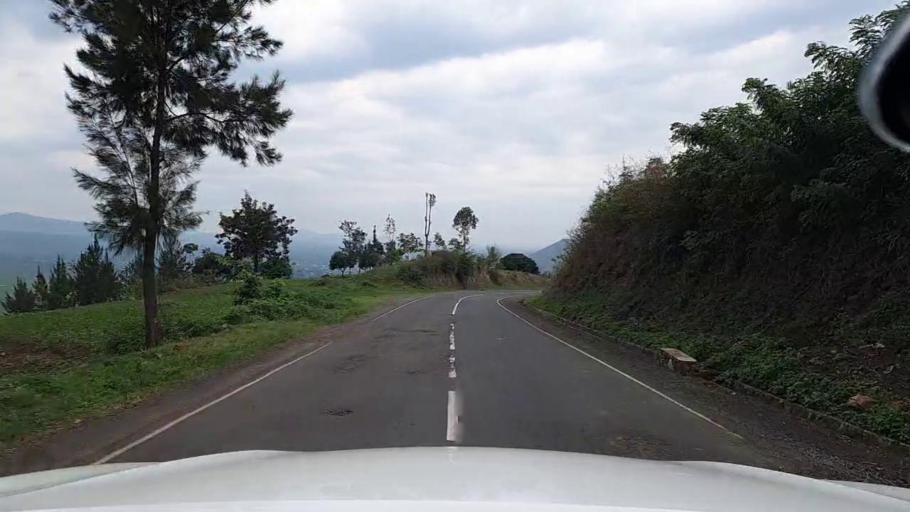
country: RW
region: Western Province
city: Cyangugu
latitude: -2.6714
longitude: 29.0038
